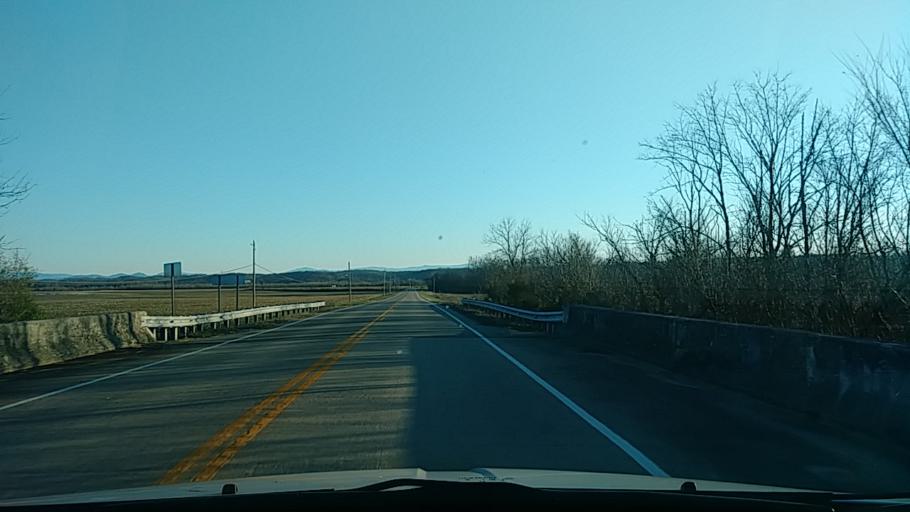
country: US
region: Tennessee
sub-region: Hamblen County
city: Morristown
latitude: 36.1735
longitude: -83.1600
